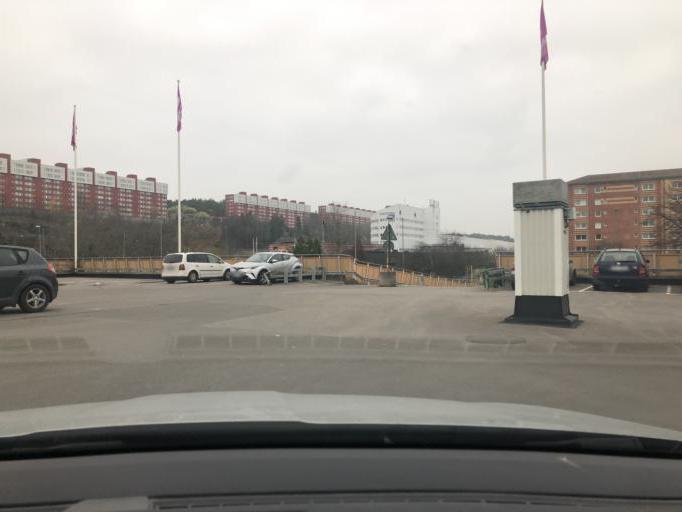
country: SE
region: Stockholm
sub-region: Botkyrka Kommun
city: Eriksberg
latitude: 59.2450
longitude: 17.8248
